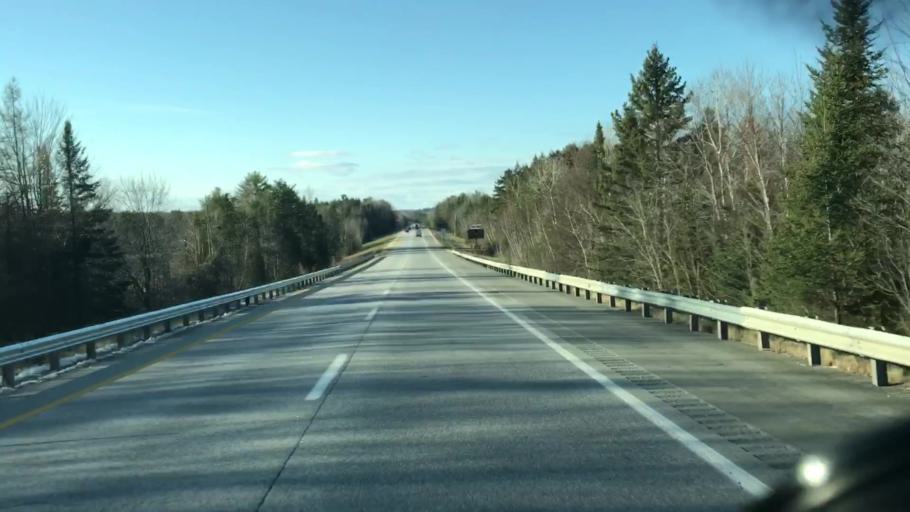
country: US
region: Maine
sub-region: Penobscot County
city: Carmel
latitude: 44.7627
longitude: -68.9856
